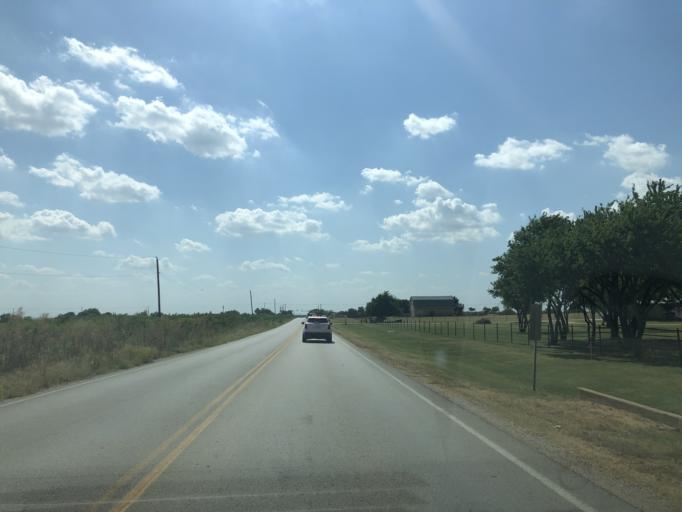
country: US
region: Texas
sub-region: Tarrant County
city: Haslet
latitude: 32.9243
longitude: -97.3445
